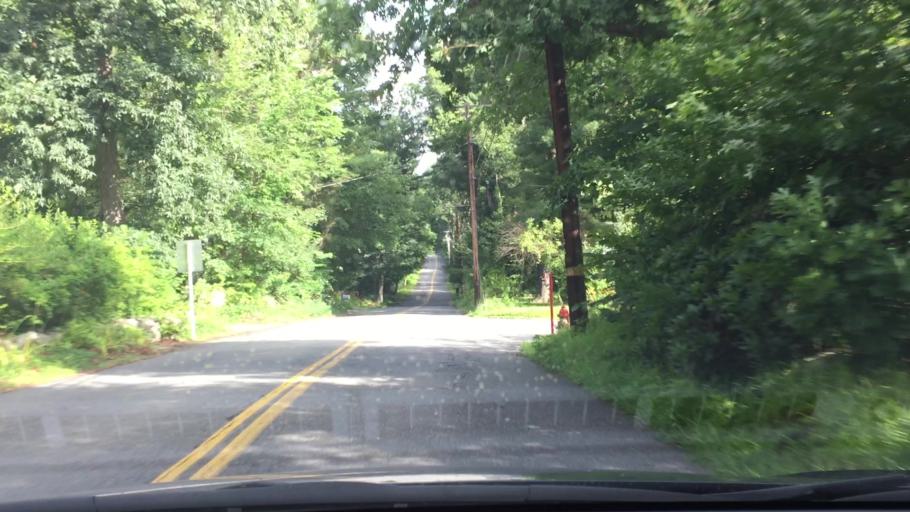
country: US
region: Massachusetts
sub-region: Middlesex County
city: Acton
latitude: 42.4907
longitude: -71.4335
